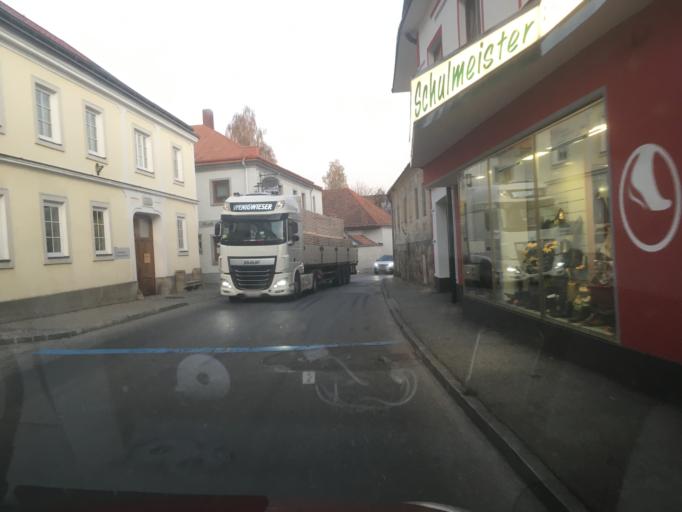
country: AT
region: Lower Austria
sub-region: Politischer Bezirk Zwettl
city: Gross-Gerungs
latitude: 48.5740
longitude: 14.9600
